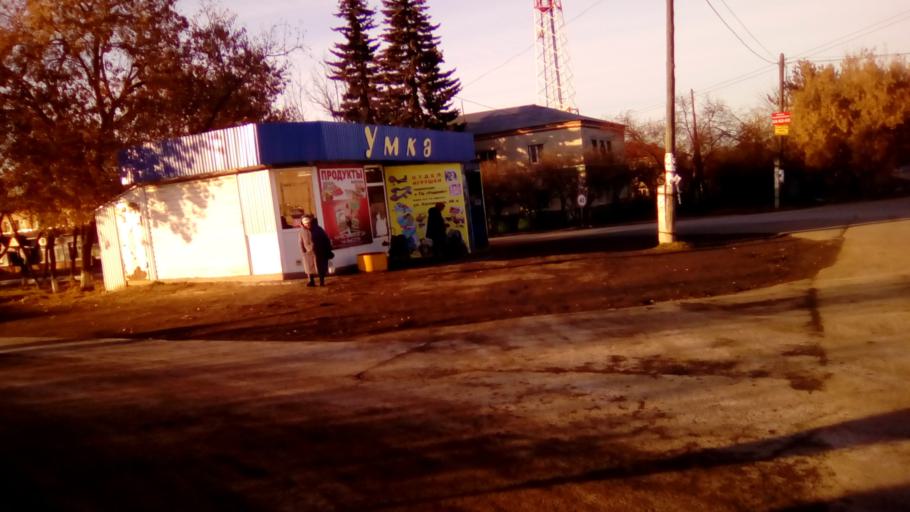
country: RU
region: Tjumen
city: Moskovskiy
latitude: 57.2201
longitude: 65.3590
